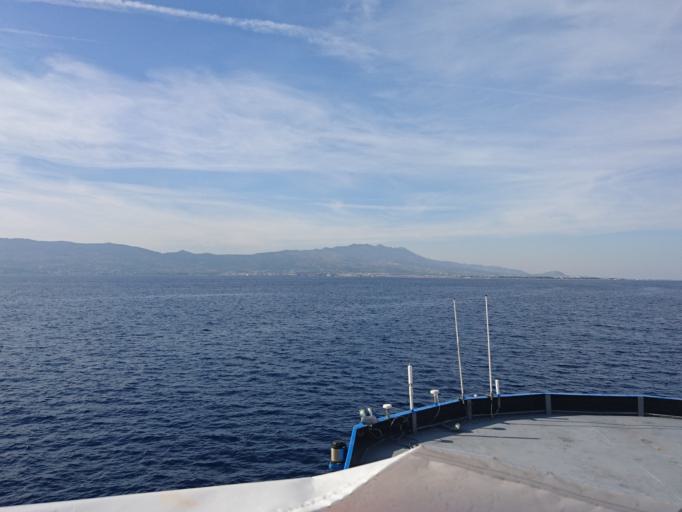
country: GR
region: South Aegean
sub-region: Nomos Dodekanisou
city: Kos
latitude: 36.9350
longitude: 27.3295
